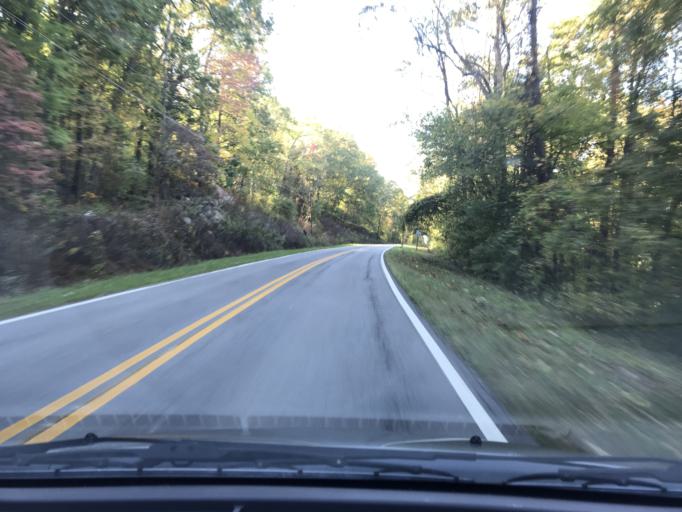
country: US
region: Georgia
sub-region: Dade County
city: Trenton
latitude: 34.8995
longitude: -85.4464
